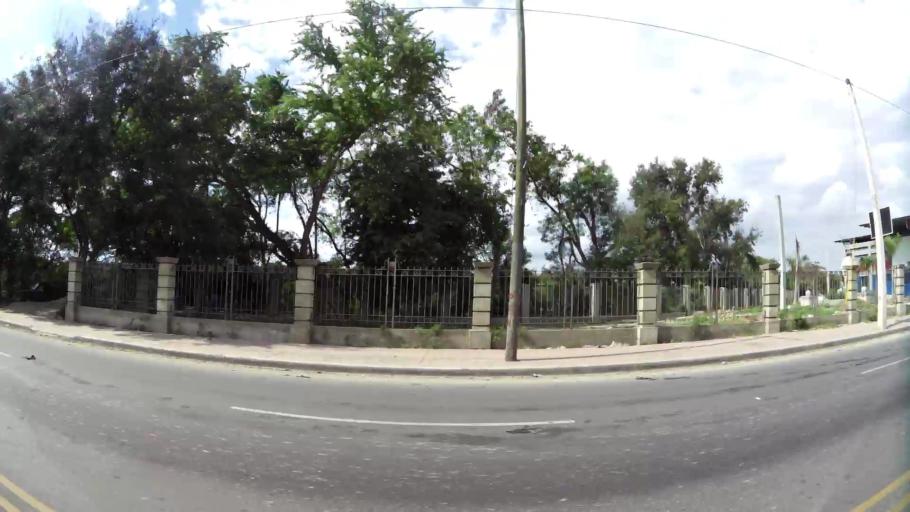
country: DO
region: Santiago
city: Santiago de los Caballeros
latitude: 19.4722
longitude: -70.7194
